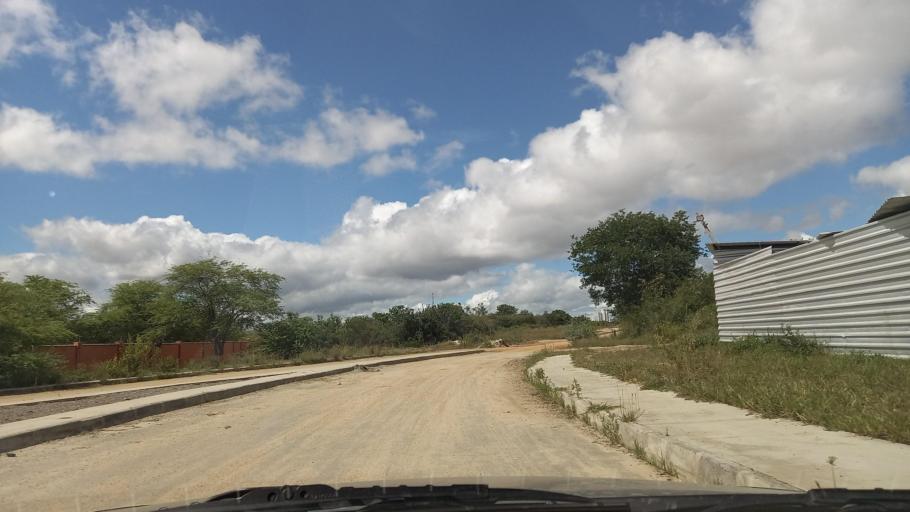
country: BR
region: Pernambuco
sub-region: Caruaru
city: Caruaru
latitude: -8.2454
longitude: -35.9830
